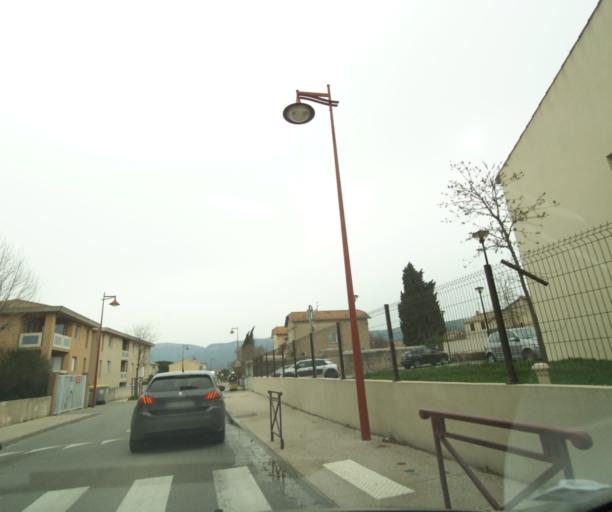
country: FR
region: Provence-Alpes-Cote d'Azur
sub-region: Departement des Bouches-du-Rhone
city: Trets
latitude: 43.4500
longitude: 5.6750
